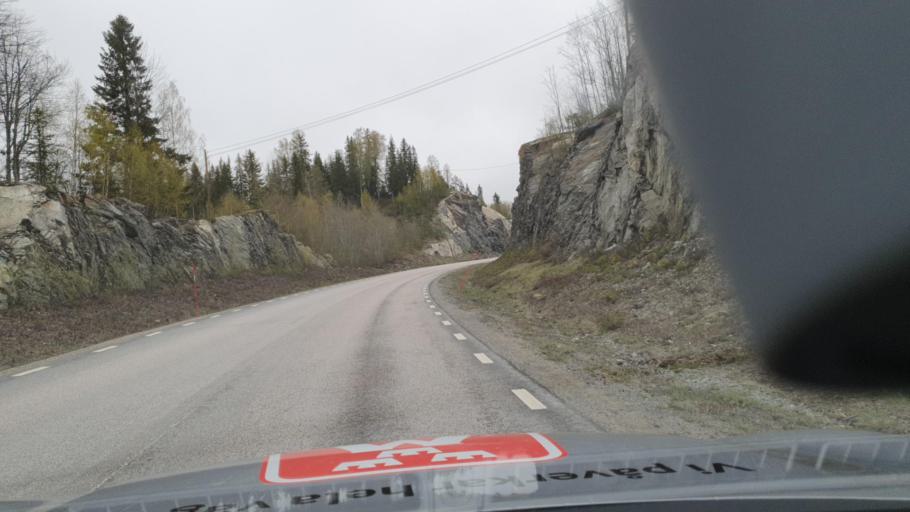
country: SE
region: Vaesternorrland
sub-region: OErnskoeldsviks Kommun
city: Ornskoldsvik
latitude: 63.3405
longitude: 18.8077
